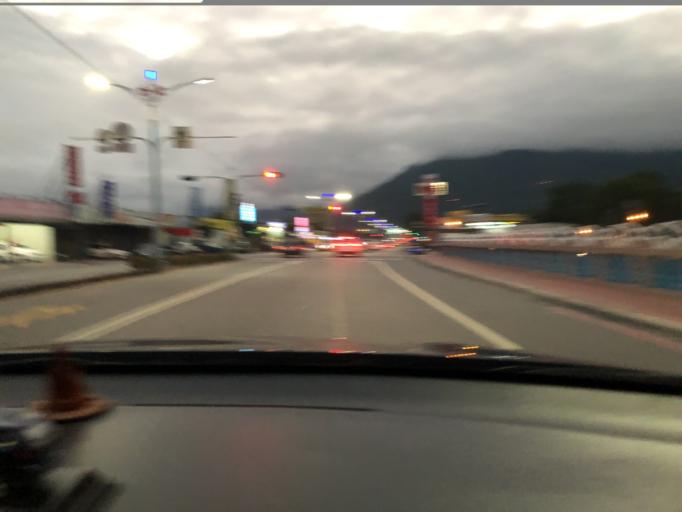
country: TW
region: Taiwan
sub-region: Hualien
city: Hualian
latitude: 23.9771
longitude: 121.5816
